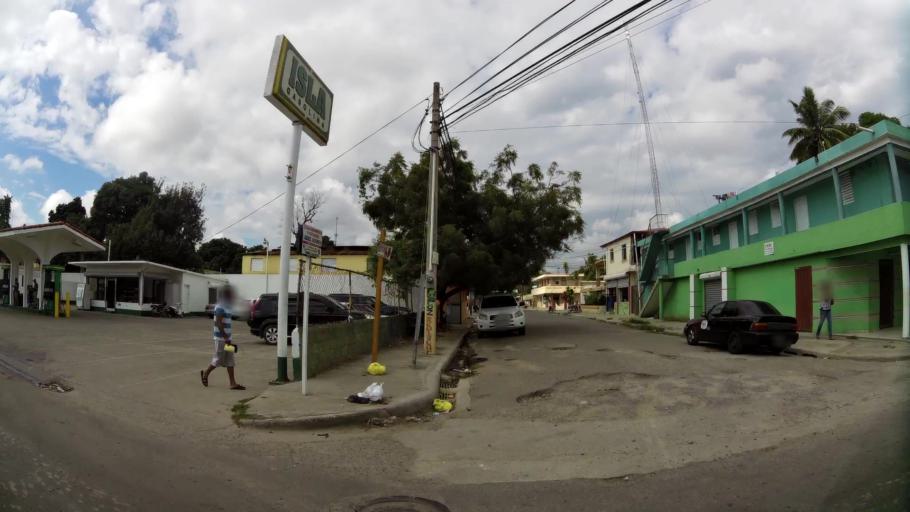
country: DO
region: Santiago
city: Santiago de los Caballeros
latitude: 19.4401
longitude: -70.7065
